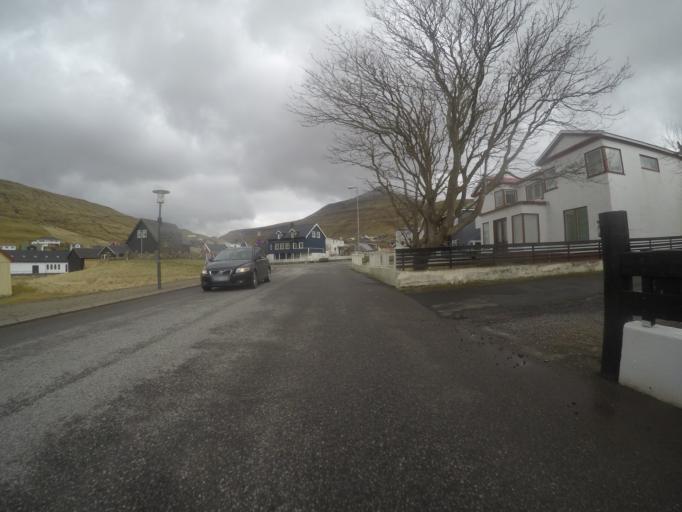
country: FO
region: Vagar
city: Midvagur
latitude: 62.0548
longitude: -7.1490
